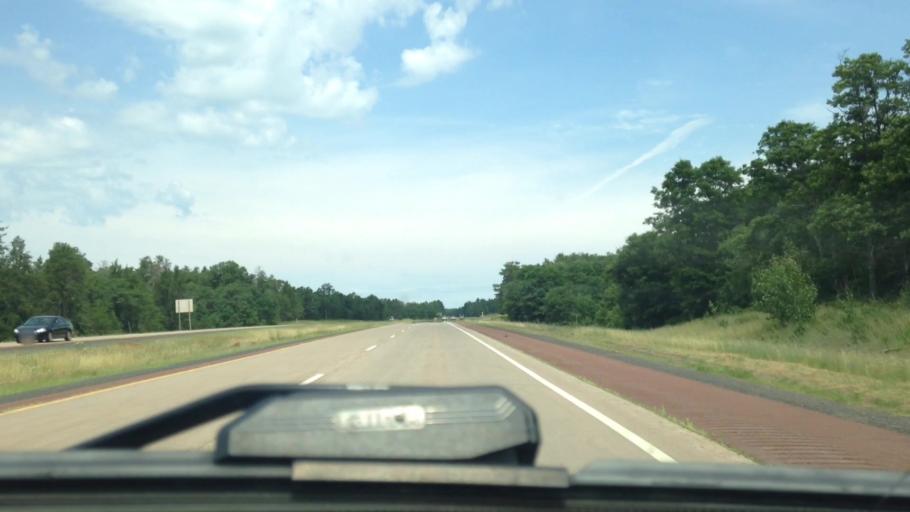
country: US
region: Wisconsin
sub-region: Douglas County
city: Lake Nebagamon
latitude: 46.3334
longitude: -91.8266
